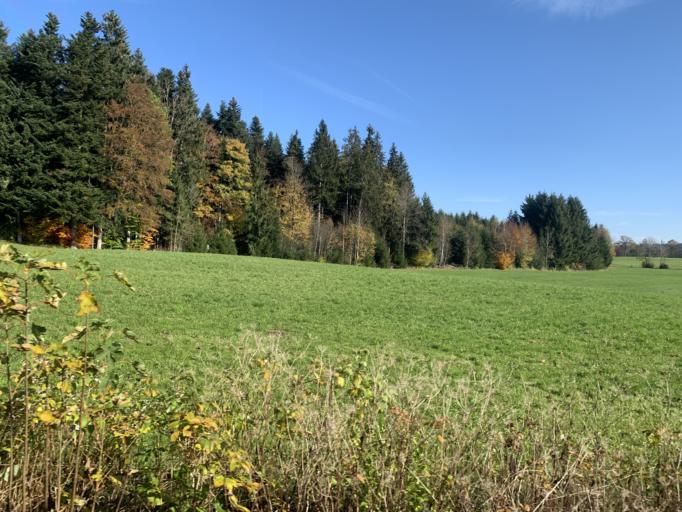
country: DE
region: Bavaria
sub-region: Upper Bavaria
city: Waakirchen
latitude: 47.7818
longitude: 11.7025
